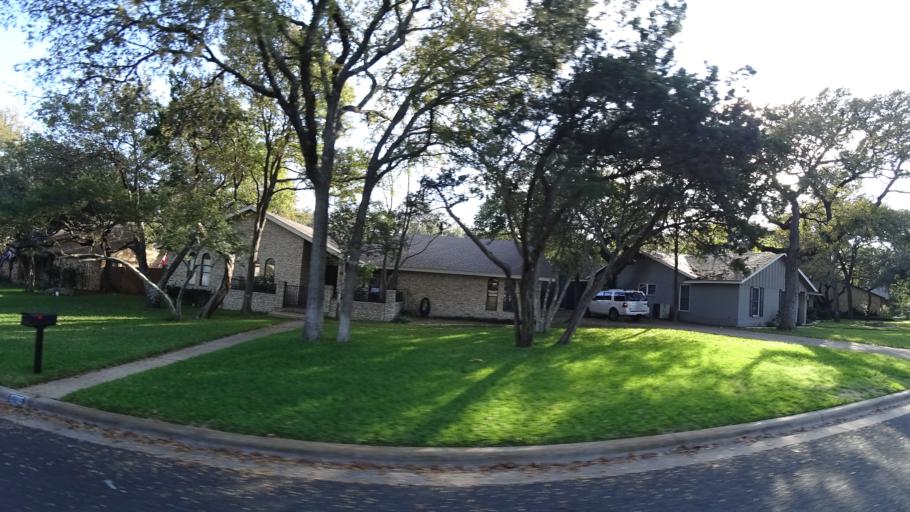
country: US
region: Texas
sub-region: Williamson County
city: Anderson Mill
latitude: 30.4303
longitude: -97.8051
